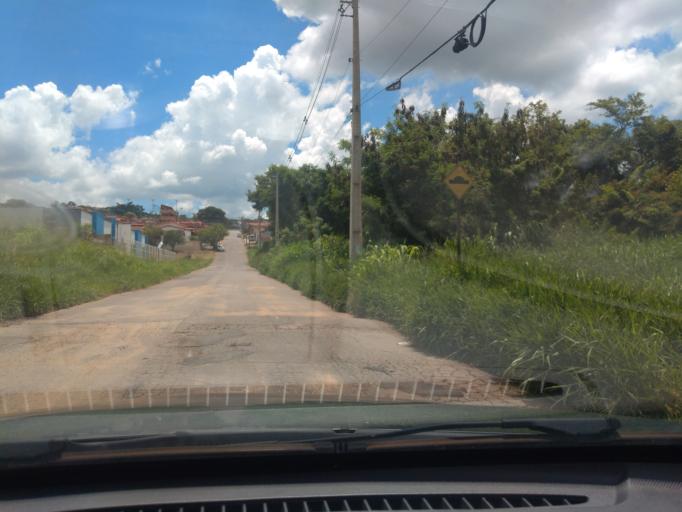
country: BR
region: Minas Gerais
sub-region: Tres Coracoes
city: Tres Coracoes
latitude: -21.6790
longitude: -45.2718
